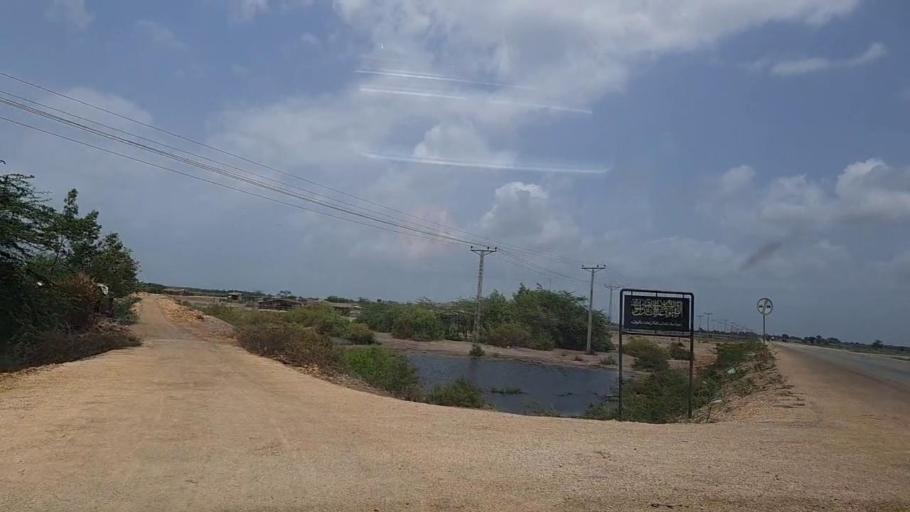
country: PK
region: Sindh
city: Thatta
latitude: 24.6199
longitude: 68.0323
